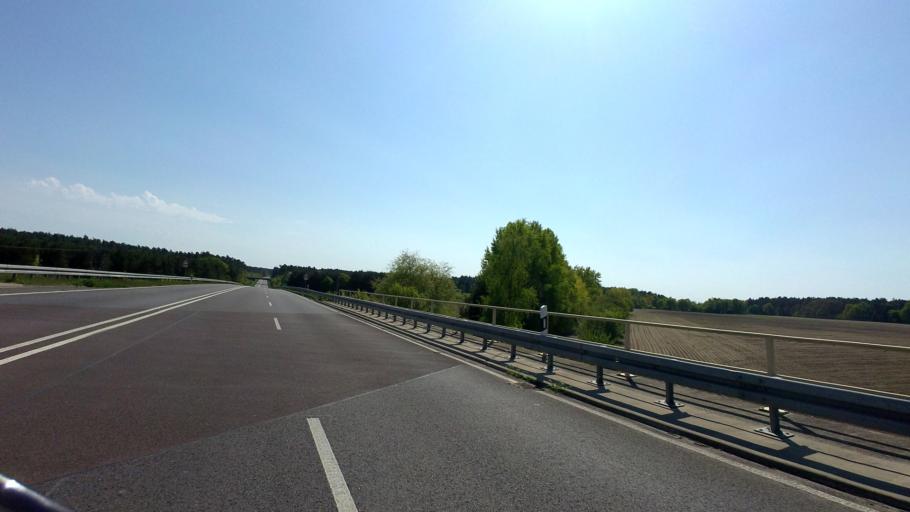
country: DE
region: Brandenburg
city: Beeskow
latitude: 52.1659
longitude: 14.2168
